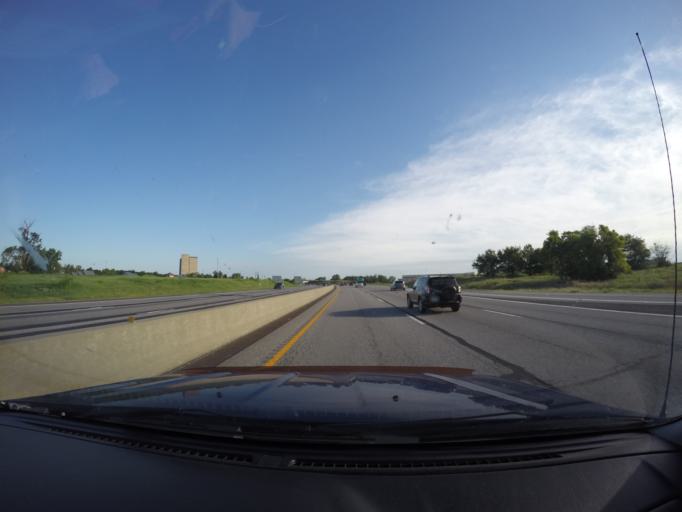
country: US
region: Missouri
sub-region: Platte County
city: Weatherby Lake
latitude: 39.2564
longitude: -94.6585
